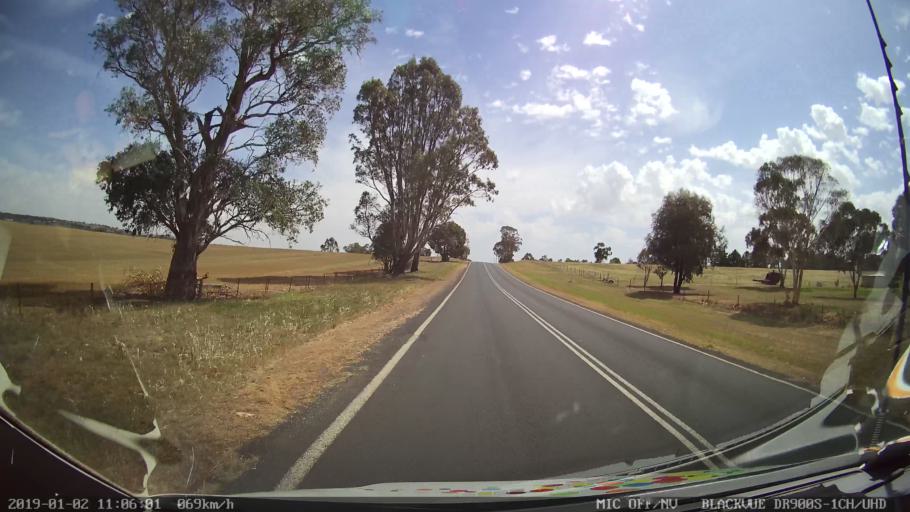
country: AU
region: New South Wales
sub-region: Young
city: Young
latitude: -34.5586
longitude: 148.3550
